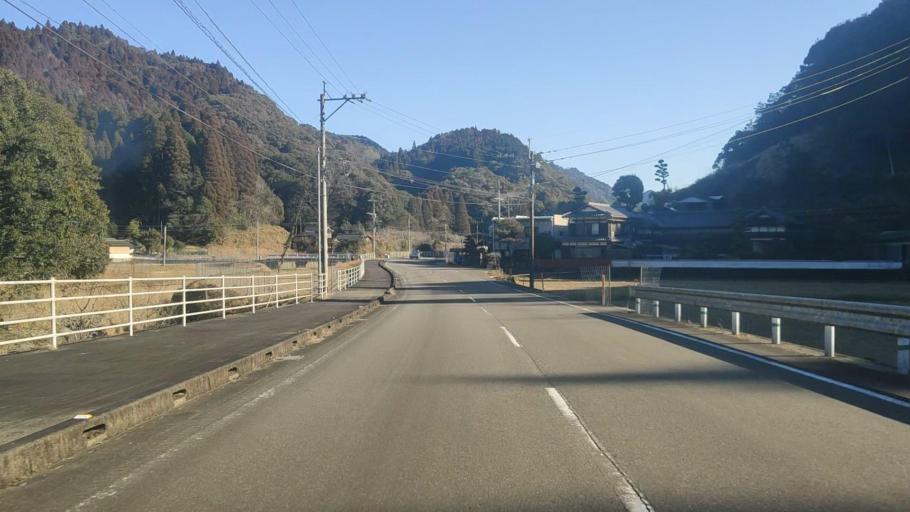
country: JP
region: Oita
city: Saiki
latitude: 32.7698
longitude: 131.8049
